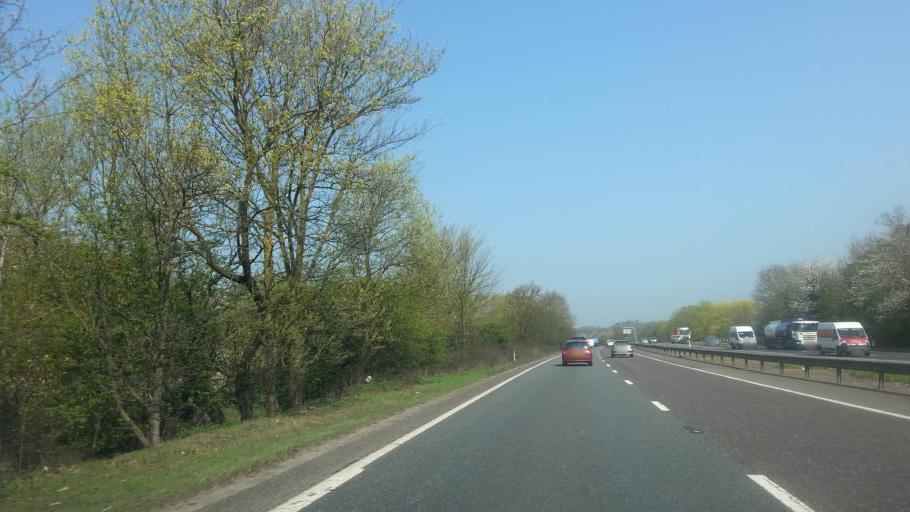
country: GB
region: England
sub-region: Suffolk
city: Bramford
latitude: 52.1207
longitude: 1.1003
